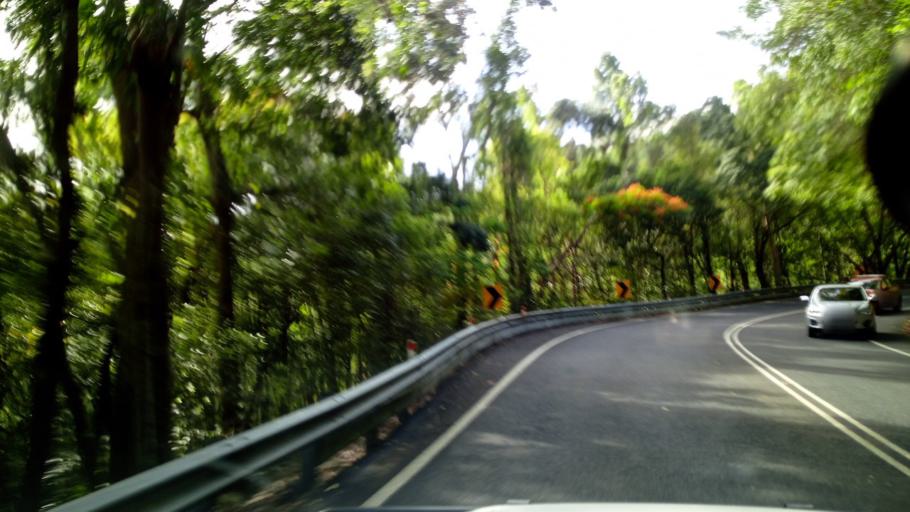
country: AU
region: Queensland
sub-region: Cairns
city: Redlynch
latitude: -16.8426
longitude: 145.6804
